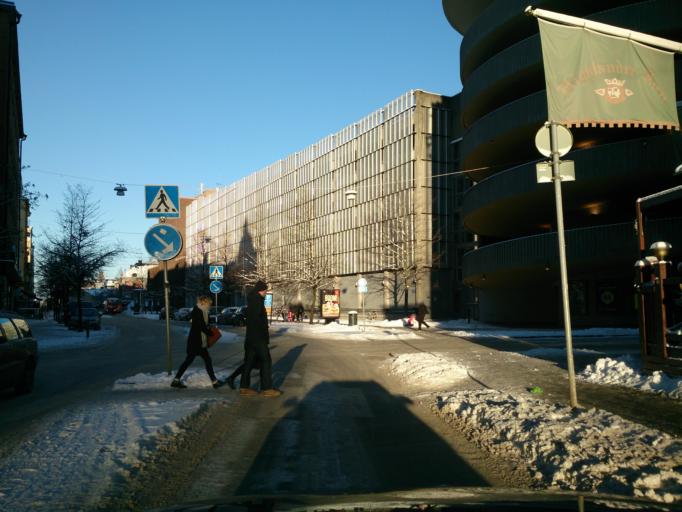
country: SE
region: OEstergoetland
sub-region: Norrkopings Kommun
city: Norrkoping
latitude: 58.5860
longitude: 16.1879
